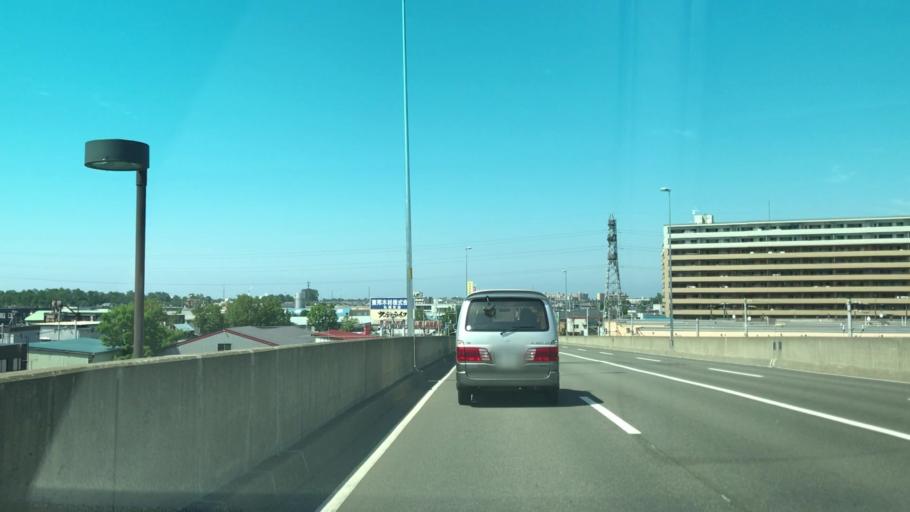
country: JP
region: Hokkaido
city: Sapporo
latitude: 43.1249
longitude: 141.2359
